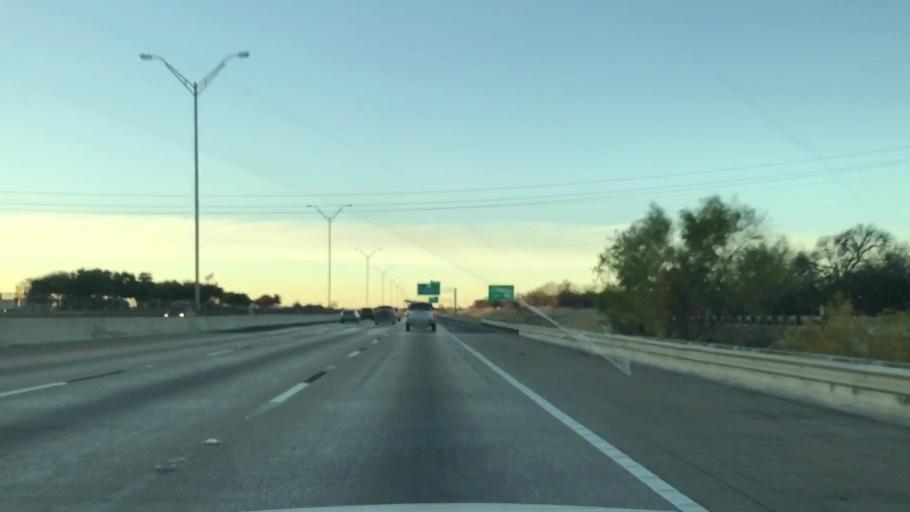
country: US
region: Texas
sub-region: Tarrant County
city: Crowley
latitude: 32.5898
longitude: -97.3200
